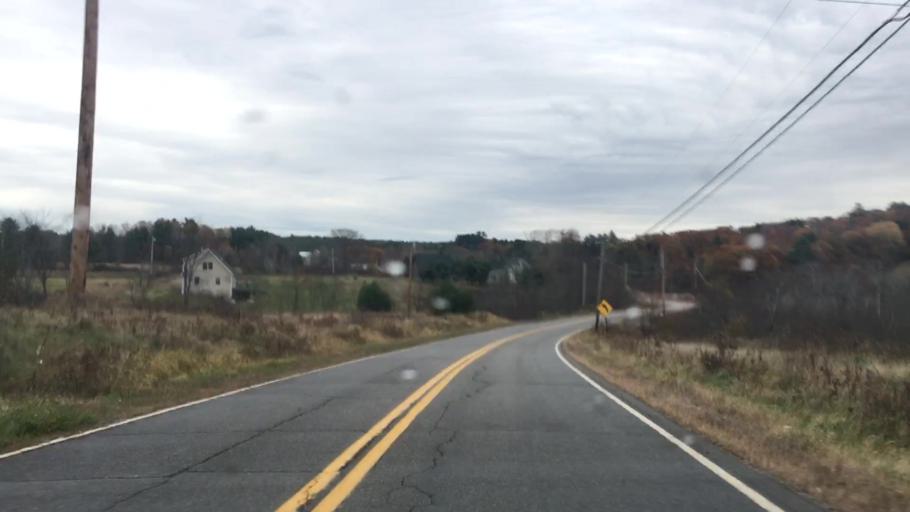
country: US
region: Maine
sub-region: Lincoln County
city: Whitefield
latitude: 44.1688
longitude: -69.6346
